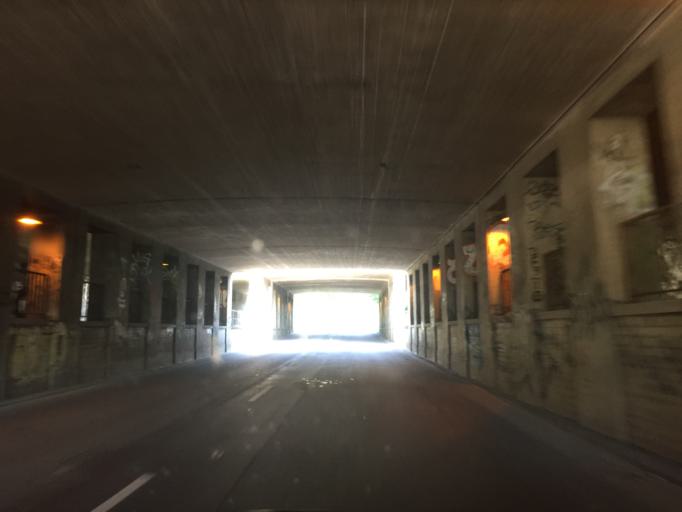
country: DK
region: Capital Region
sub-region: Frederiksberg Kommune
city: Frederiksberg
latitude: 55.7113
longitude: 12.5532
